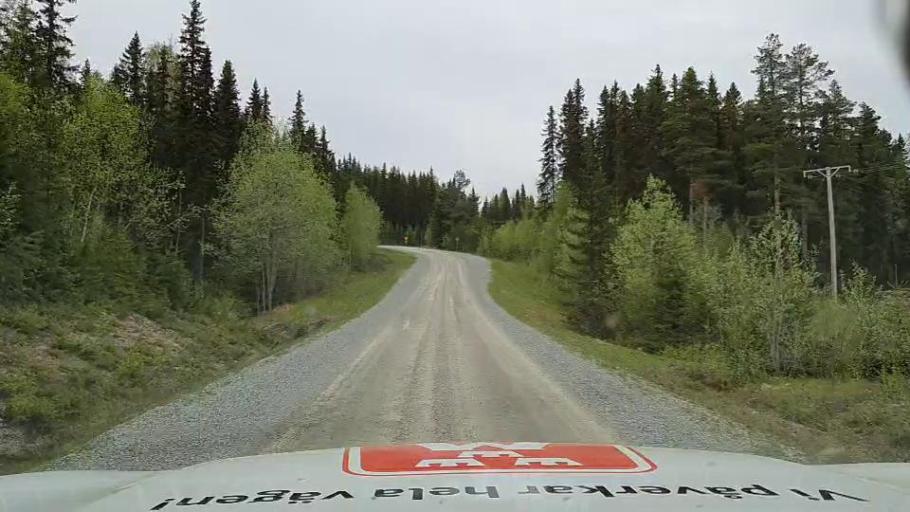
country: SE
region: Jaemtland
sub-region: OEstersunds Kommun
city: Brunflo
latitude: 62.6511
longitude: 14.9250
